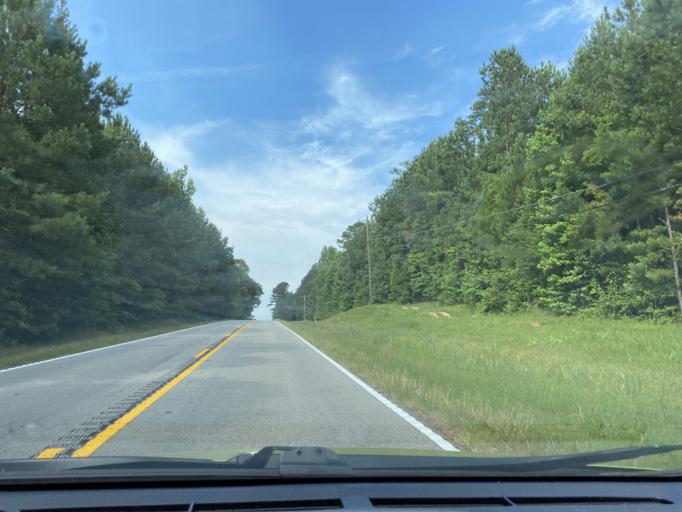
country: US
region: Georgia
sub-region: Coweta County
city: East Newnan
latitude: 33.2881
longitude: -84.6948
